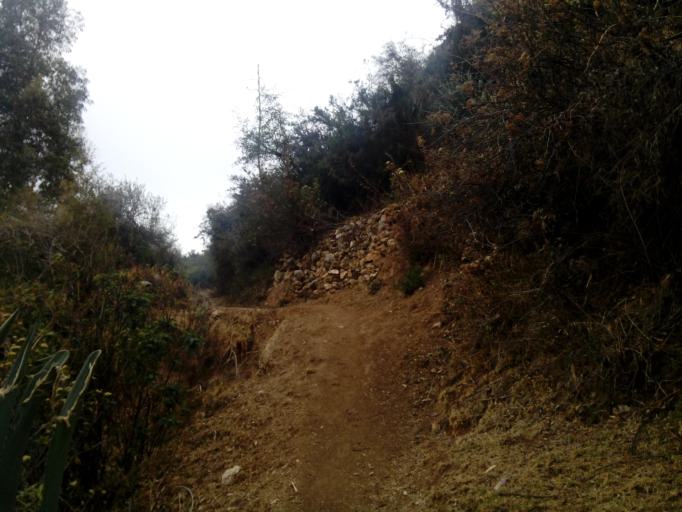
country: PE
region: Ayacucho
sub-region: Provincia de Victor Fajardo
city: Canaria
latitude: -13.9021
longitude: -73.9324
